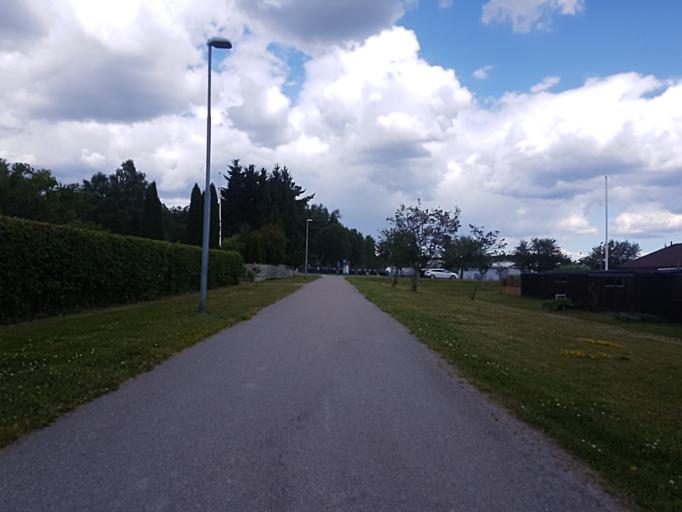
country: SE
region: Soedermanland
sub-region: Gnesta Kommun
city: Gnesta
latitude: 59.0382
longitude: 17.3266
